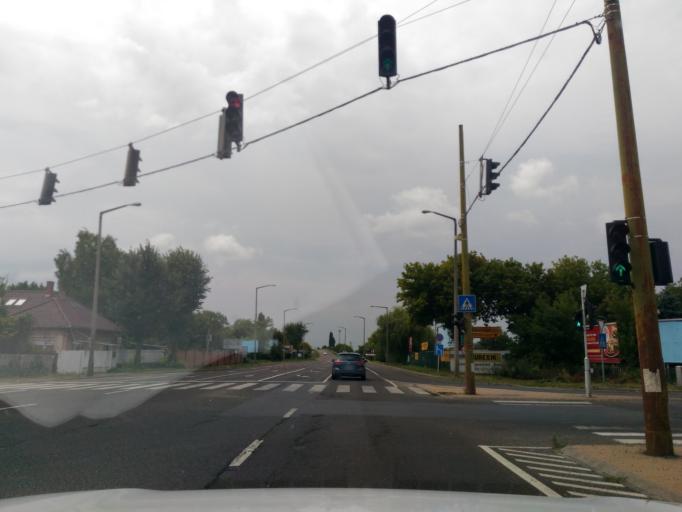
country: HU
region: Jasz-Nagykun-Szolnok
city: Szolnok
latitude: 47.1773
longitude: 20.1538
